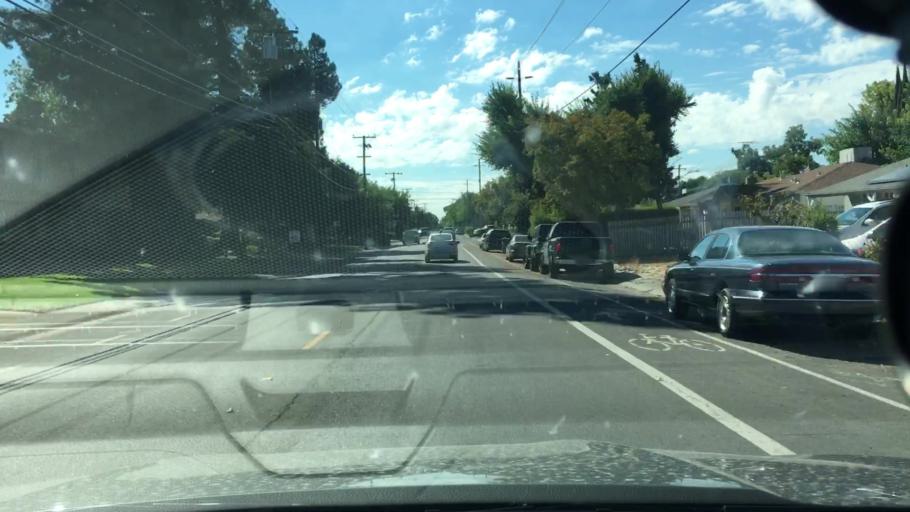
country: US
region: California
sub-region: Sacramento County
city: Arden-Arcade
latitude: 38.5931
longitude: -121.3923
